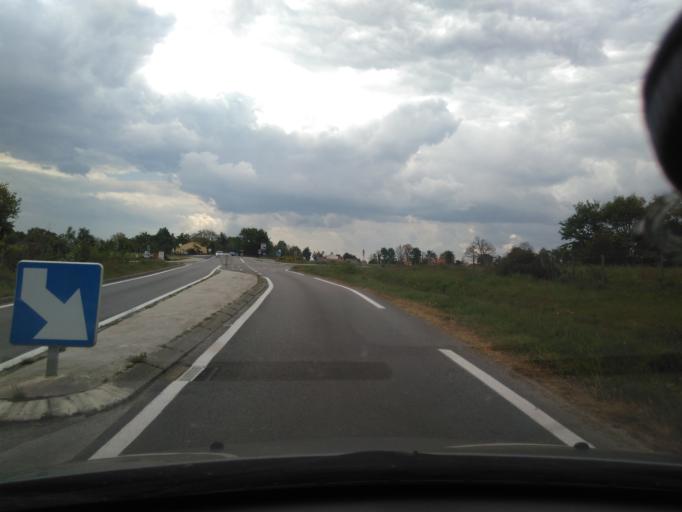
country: FR
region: Pays de la Loire
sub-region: Departement de la Vendee
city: Dompierre-sur-Yon
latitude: 46.7111
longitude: -1.4140
